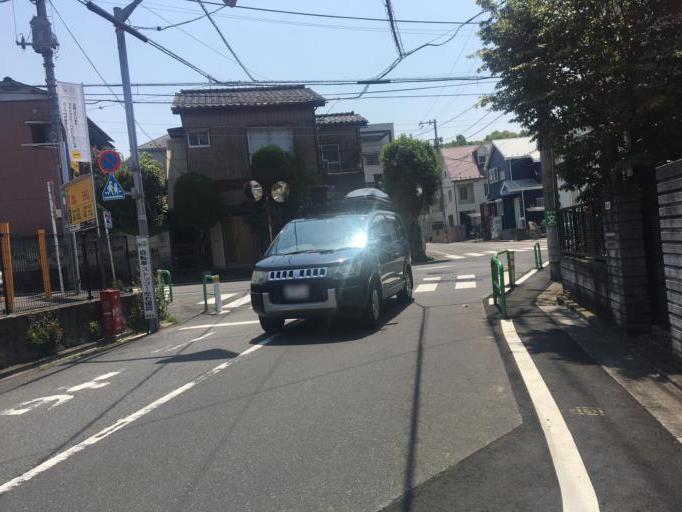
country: JP
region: Saitama
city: Wako
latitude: 35.7710
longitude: 139.6271
